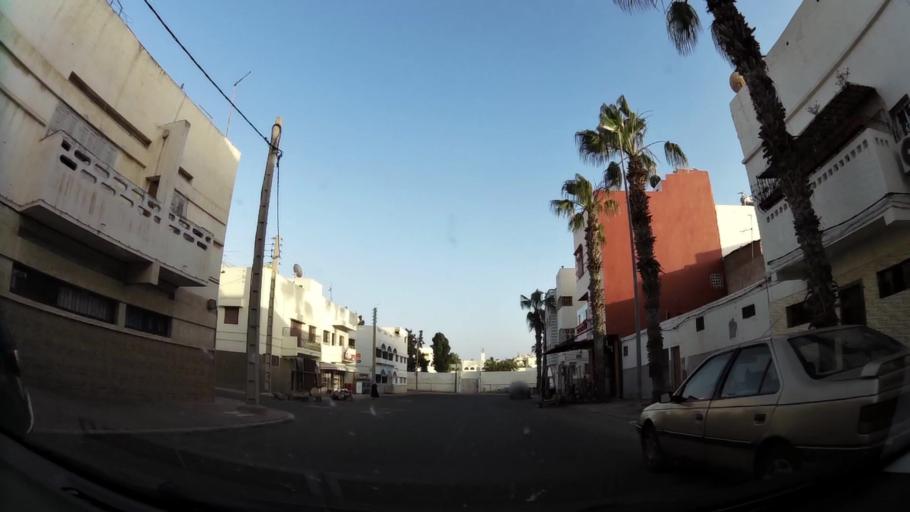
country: MA
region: Souss-Massa-Draa
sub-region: Agadir-Ida-ou-Tnan
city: Agadir
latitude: 30.4124
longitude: -9.5826
